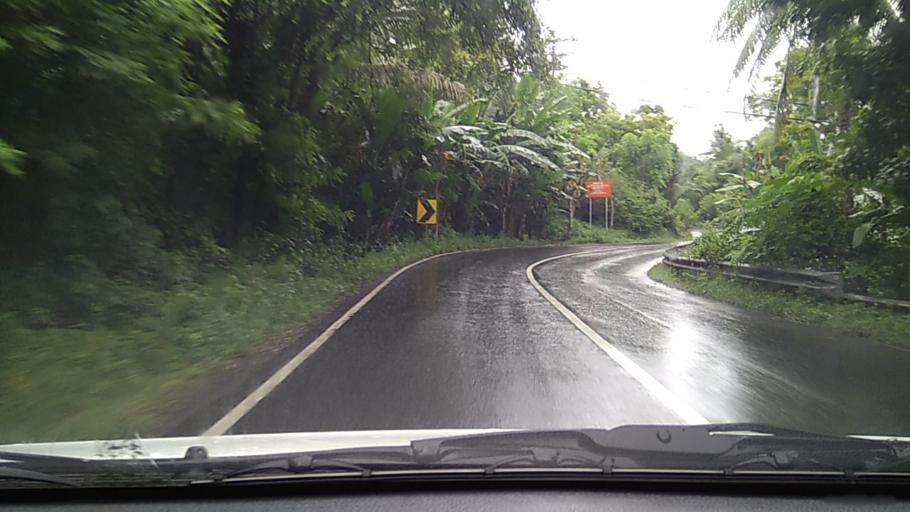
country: ID
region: Bali
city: Banjar Bugbug
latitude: -8.4993
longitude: 115.5824
